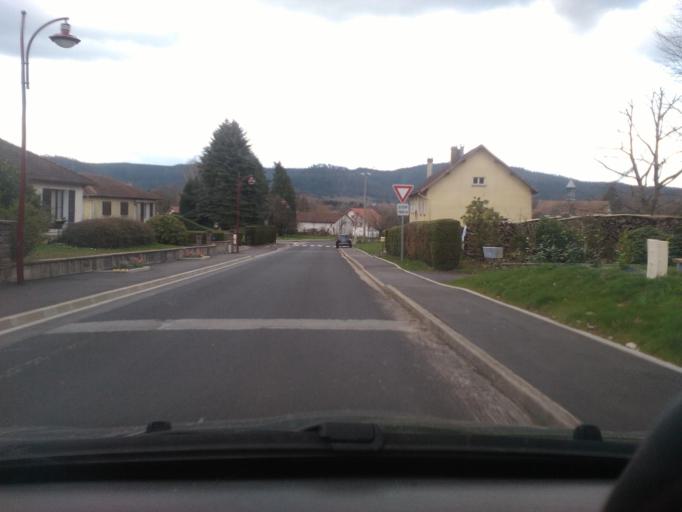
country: FR
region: Lorraine
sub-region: Departement des Vosges
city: Etival-Clairefontaine
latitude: 48.3248
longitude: 6.8274
